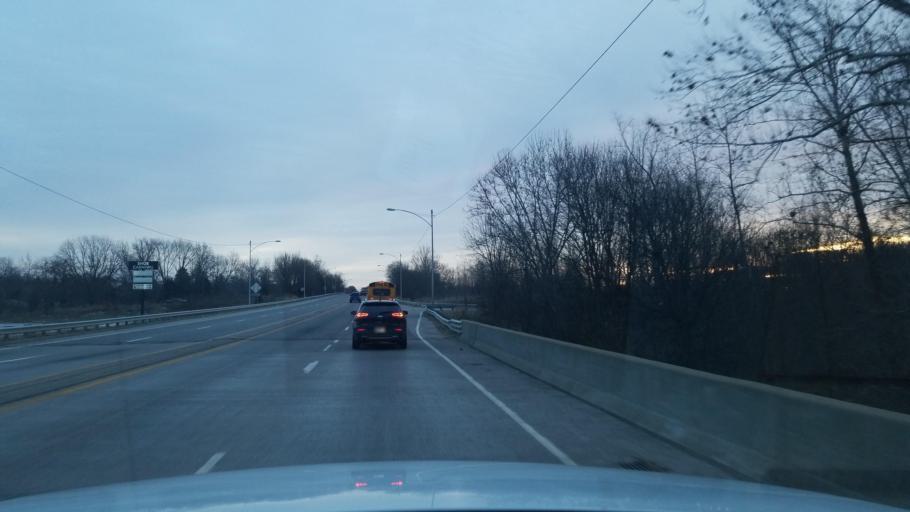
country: US
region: Indiana
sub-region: Vanderburgh County
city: Evansville
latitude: 37.9776
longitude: -87.6251
